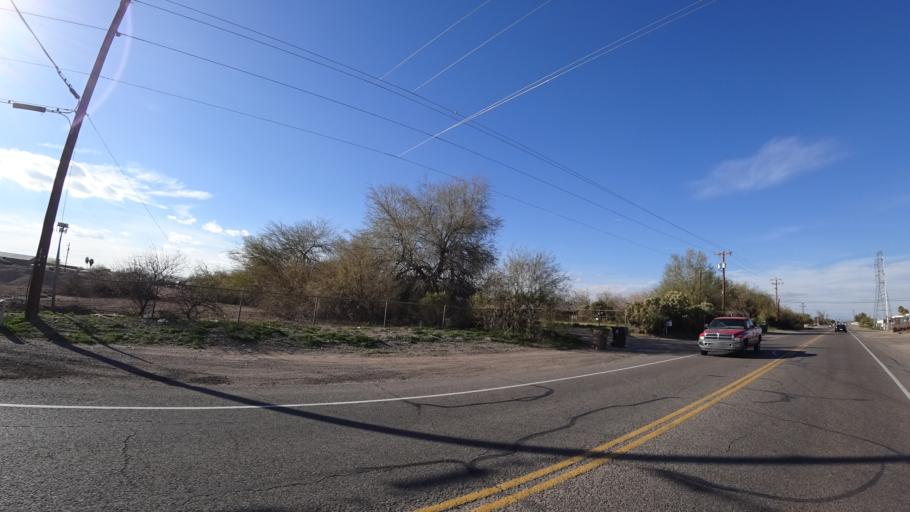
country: US
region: Arizona
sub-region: Maricopa County
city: Peoria
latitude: 33.5540
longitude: -112.2379
